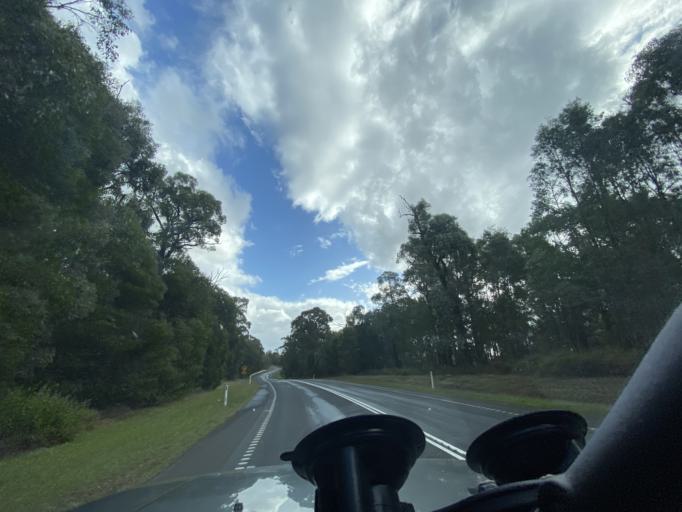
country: AU
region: Victoria
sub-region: Murrindindi
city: Kinglake West
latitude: -37.4902
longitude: 145.2120
